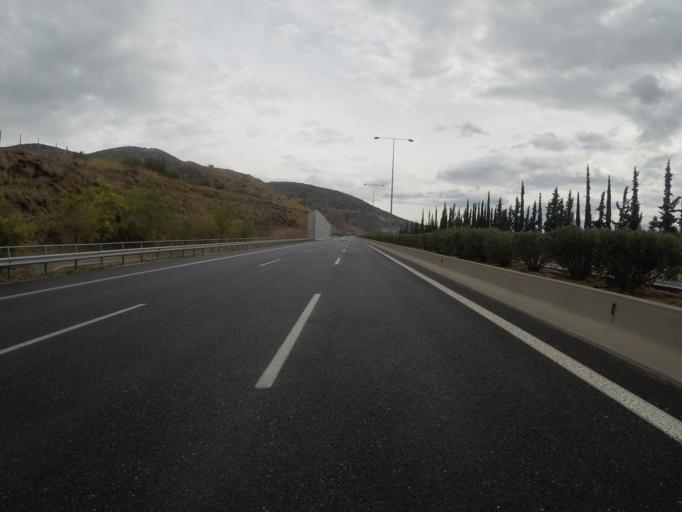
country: GR
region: Attica
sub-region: Nomarchia Dytikis Attikis
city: Fyli
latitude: 38.0866
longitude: 23.6475
